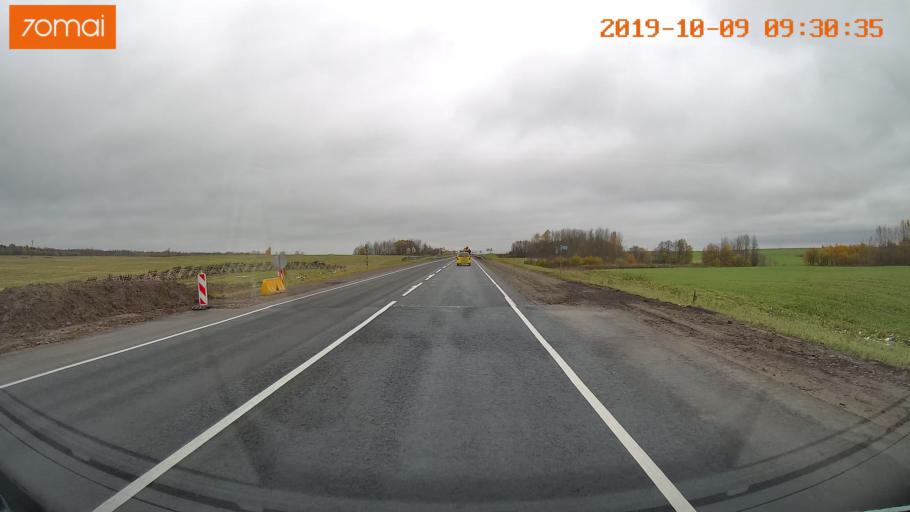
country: RU
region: Vologda
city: Vologda
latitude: 59.1411
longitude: 39.9477
